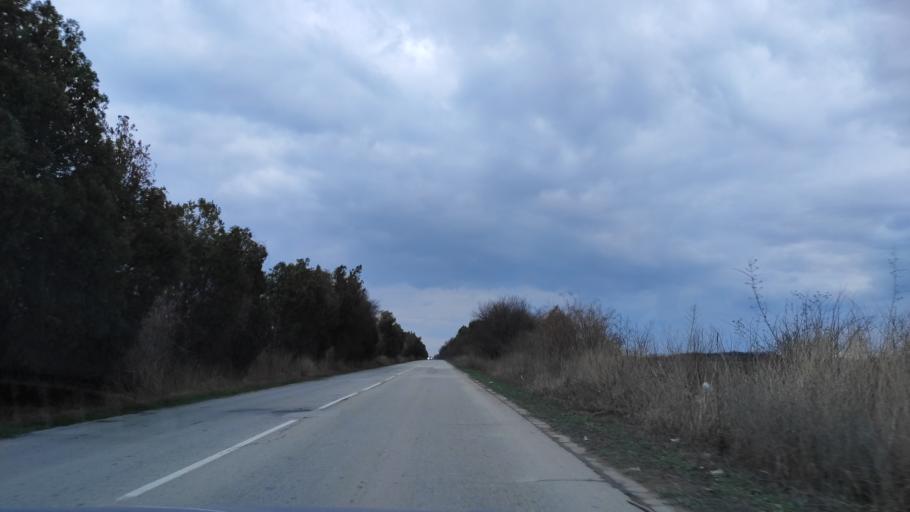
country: BG
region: Varna
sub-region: Obshtina Aksakovo
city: Aksakovo
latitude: 43.2298
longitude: 27.8120
